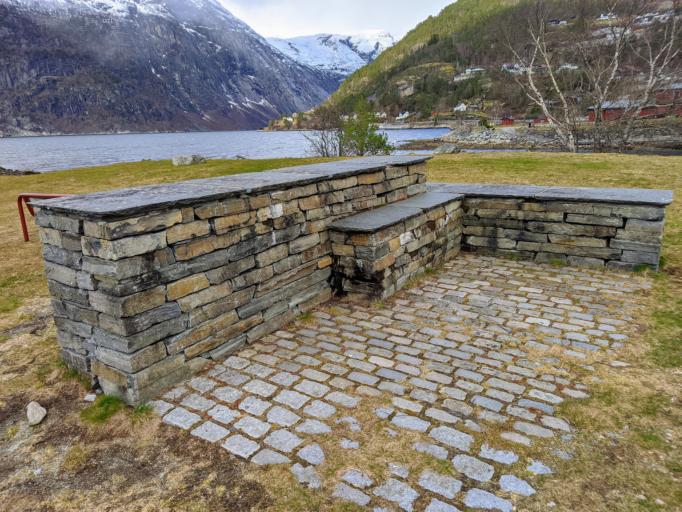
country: NO
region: Hordaland
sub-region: Eidfjord
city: Eidfjord
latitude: 60.4689
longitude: 7.0693
